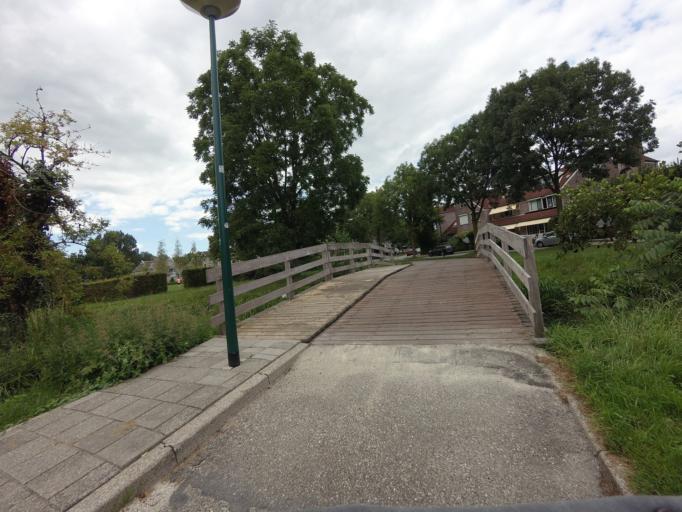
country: NL
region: Utrecht
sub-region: Gemeente IJsselstein
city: IJsselstein
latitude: 52.0231
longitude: 5.0245
